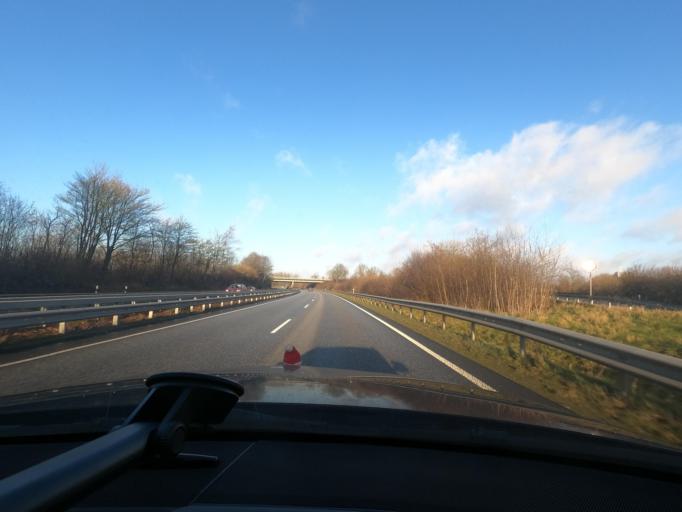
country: DE
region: Schleswig-Holstein
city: Jarplund-Weding
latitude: 54.7555
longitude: 9.4305
